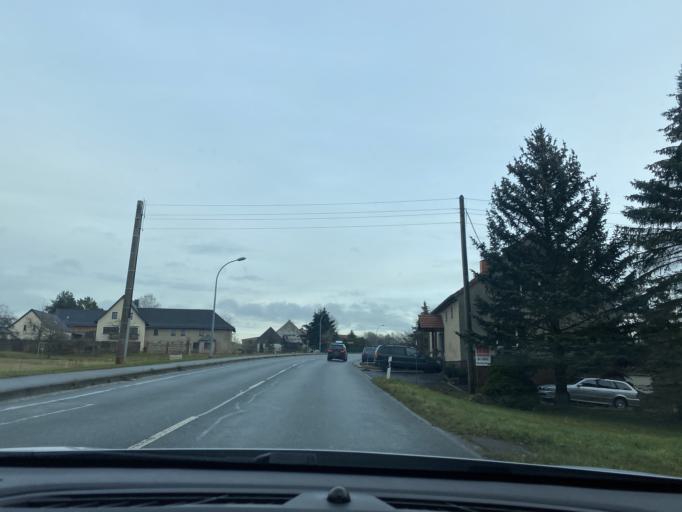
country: DE
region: Saxony
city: Reichenbach
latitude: 51.1449
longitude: 14.8109
